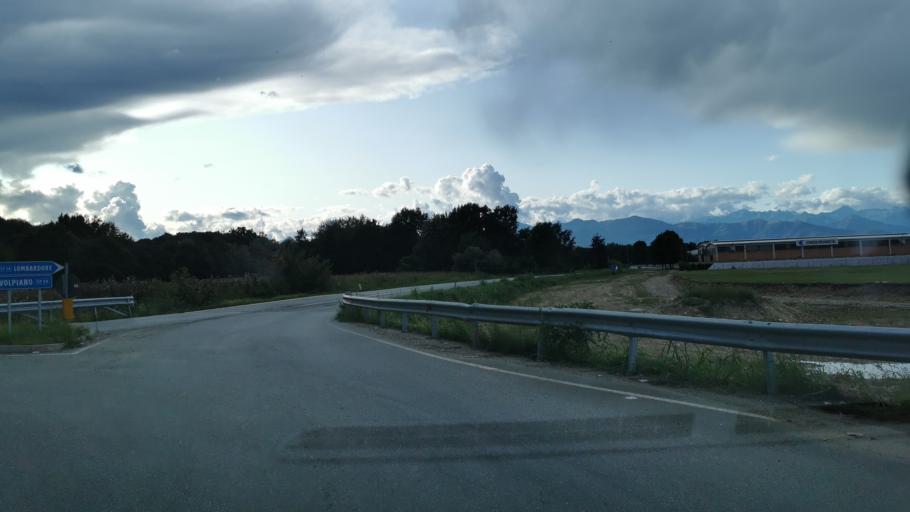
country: IT
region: Piedmont
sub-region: Provincia di Torino
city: Lombardore
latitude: 45.2287
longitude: 7.7548
